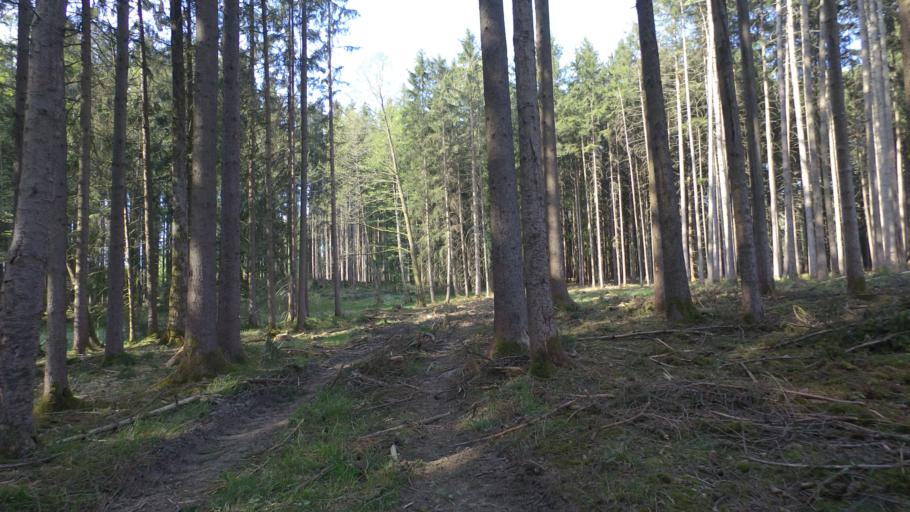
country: DE
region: Bavaria
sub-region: Upper Bavaria
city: Chieming
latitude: 47.9170
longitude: 12.5101
